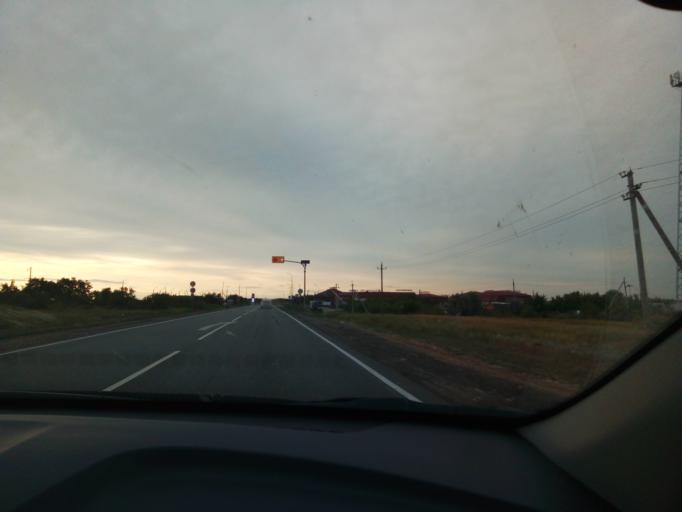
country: RU
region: Volgograd
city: Primorsk
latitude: 49.2636
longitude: 44.8810
